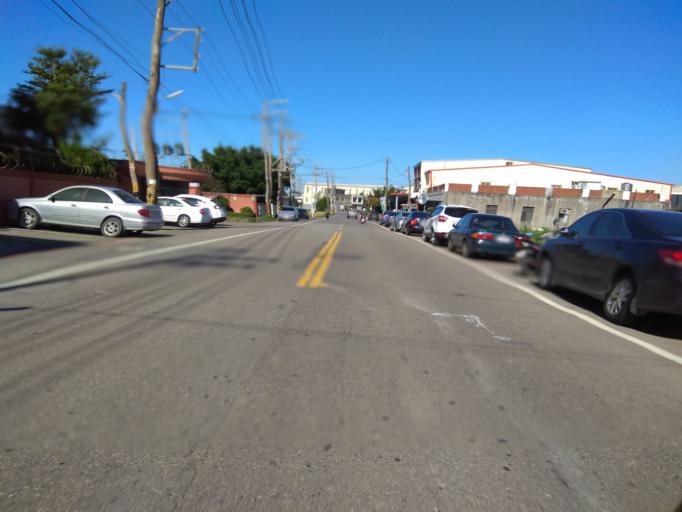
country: TW
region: Taiwan
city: Taoyuan City
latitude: 24.9756
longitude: 121.1377
